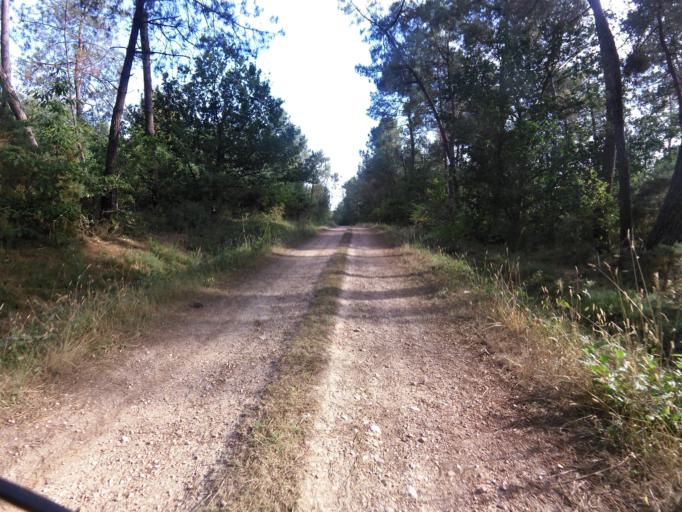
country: FR
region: Brittany
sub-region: Departement du Morbihan
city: Molac
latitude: 47.7084
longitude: -2.4174
